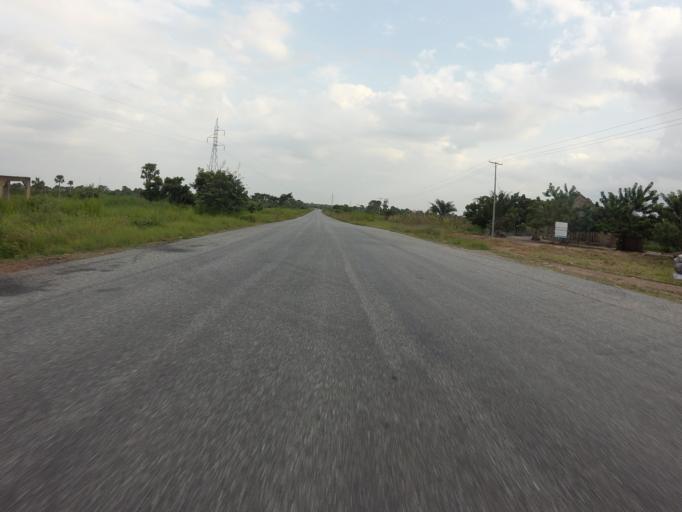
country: GH
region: Volta
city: Ho
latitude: 6.3925
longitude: 0.5261
